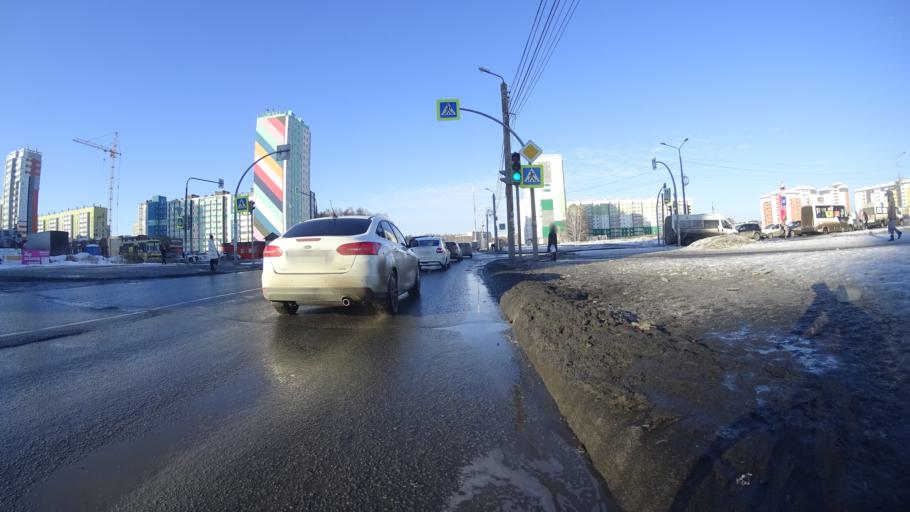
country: RU
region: Chelyabinsk
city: Roshchino
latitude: 55.2097
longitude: 61.2843
